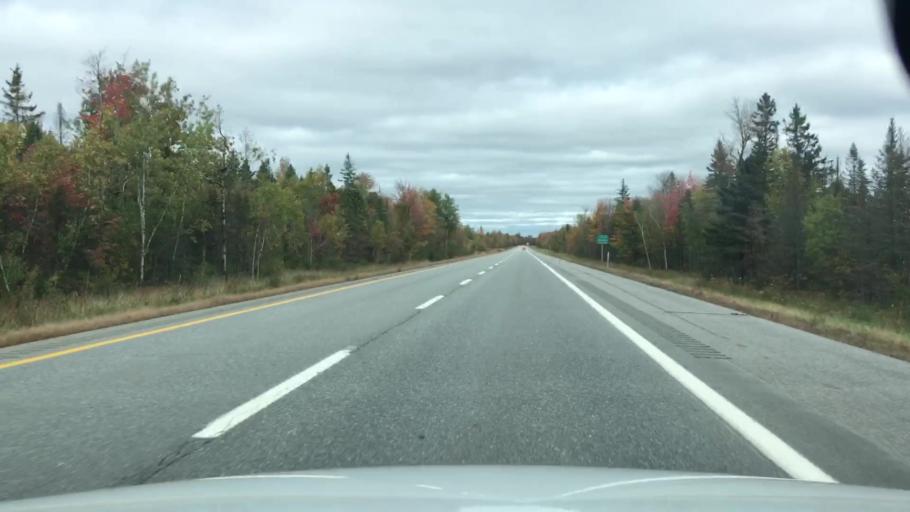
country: US
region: Maine
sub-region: Waldo County
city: Burnham
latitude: 44.6824
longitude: -69.4770
